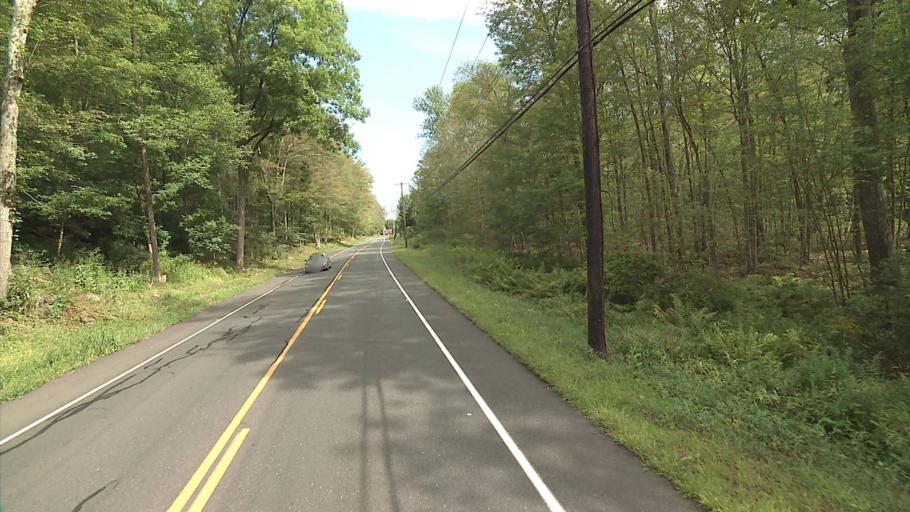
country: US
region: Connecticut
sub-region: Tolland County
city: Stafford Springs
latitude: 41.9433
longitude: -72.3056
